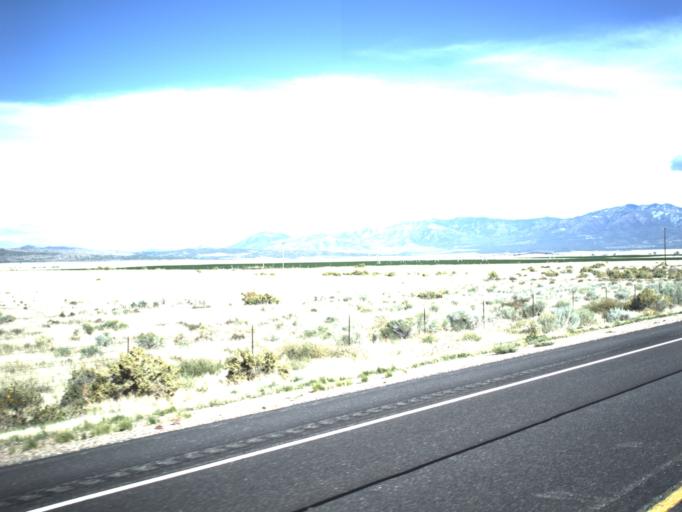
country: US
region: Utah
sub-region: Millard County
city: Fillmore
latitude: 39.1449
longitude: -112.3850
